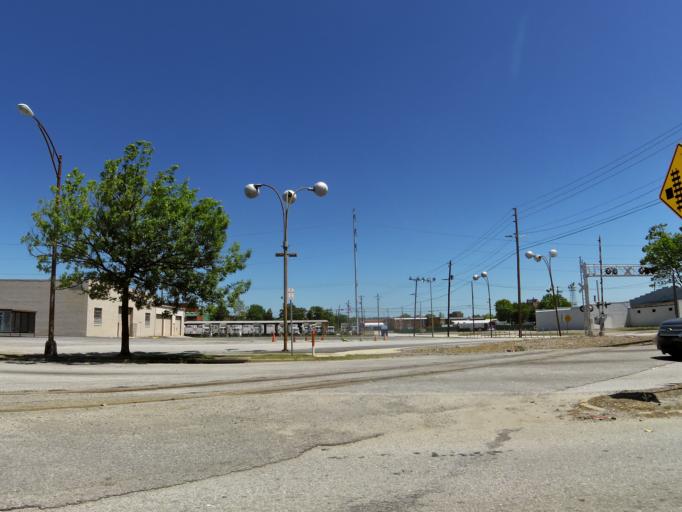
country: US
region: Georgia
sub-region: Richmond County
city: Augusta
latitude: 33.4710
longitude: -81.9766
